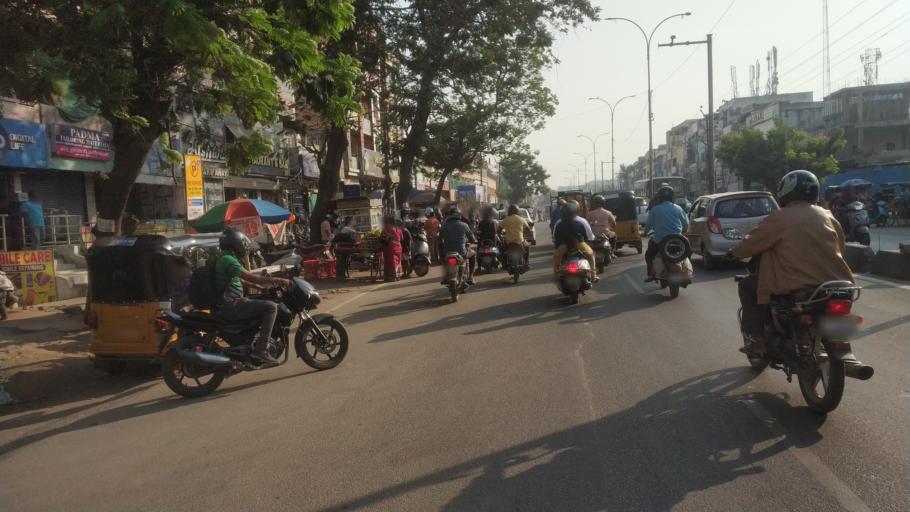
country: IN
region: Telangana
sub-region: Rangareddi
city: Quthbullapur
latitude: 17.4921
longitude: 78.4515
